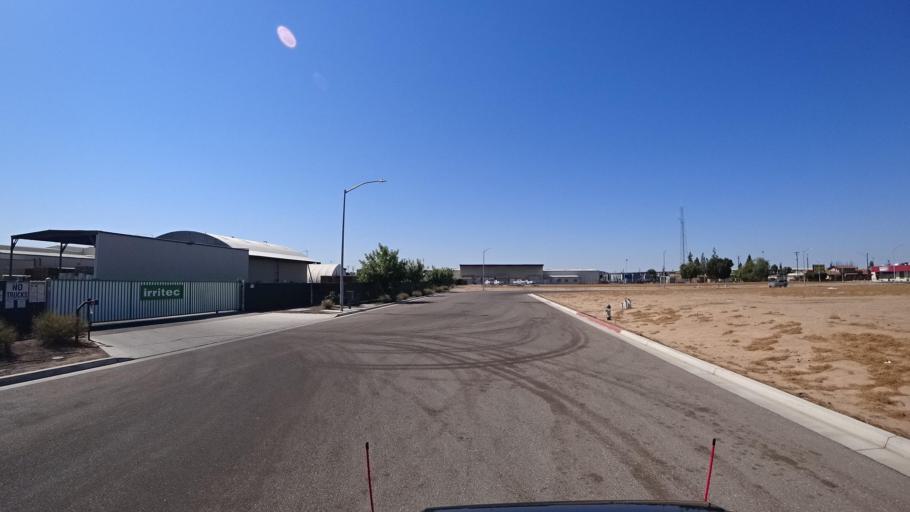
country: US
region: California
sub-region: Fresno County
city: Fresno
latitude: 36.7625
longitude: -119.7440
